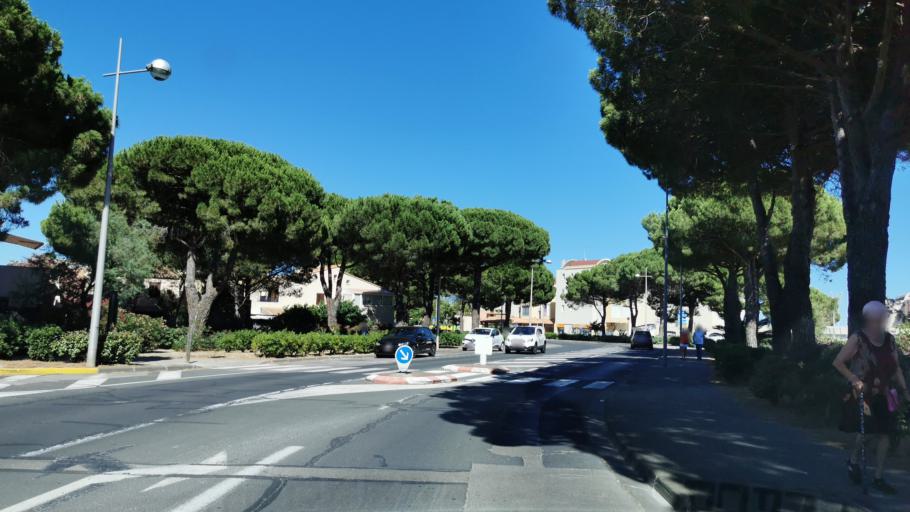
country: FR
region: Languedoc-Roussillon
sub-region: Departement de l'Aude
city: Gruissan
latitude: 43.1108
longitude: 3.1004
